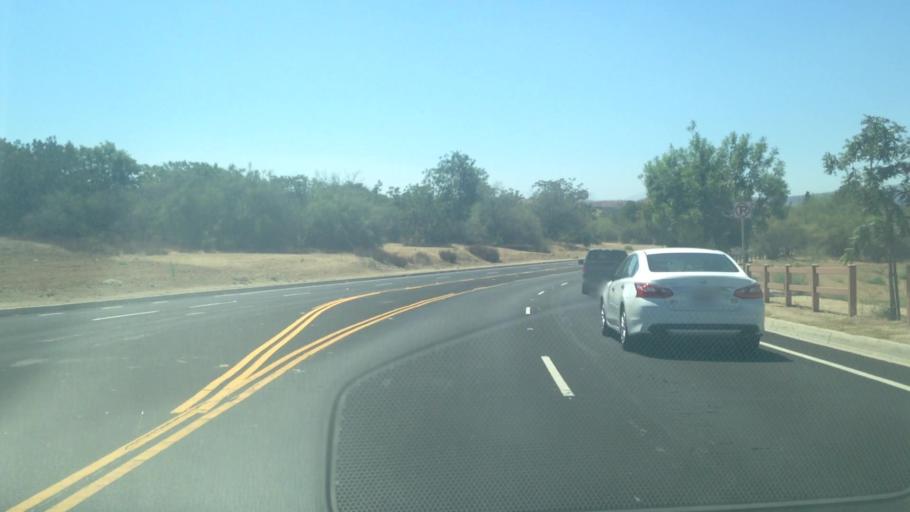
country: US
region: California
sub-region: Riverside County
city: Calimesa
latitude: 34.0252
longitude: -117.0821
